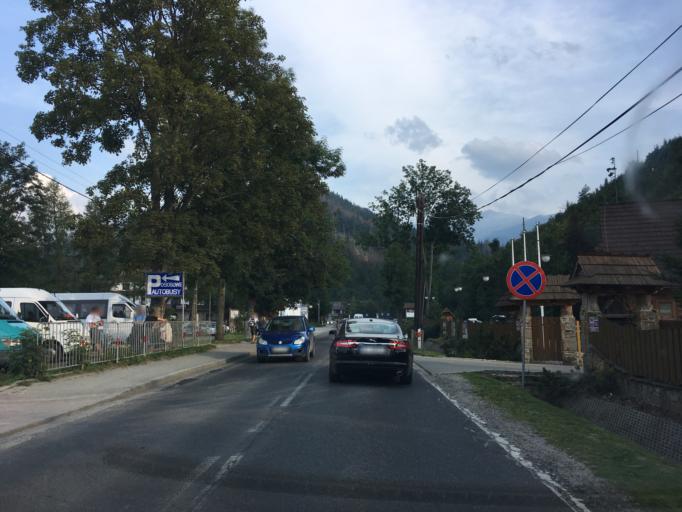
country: PL
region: Lesser Poland Voivodeship
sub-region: Powiat tatrzanski
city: Koscielisko
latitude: 49.2772
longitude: 19.8658
